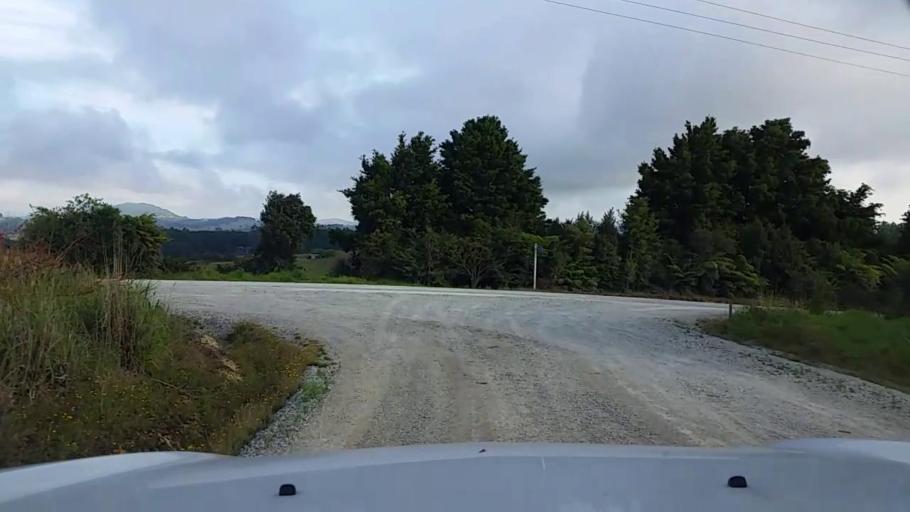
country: NZ
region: Northland
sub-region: Whangarei
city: Maungatapere
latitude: -35.6680
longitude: 174.1744
